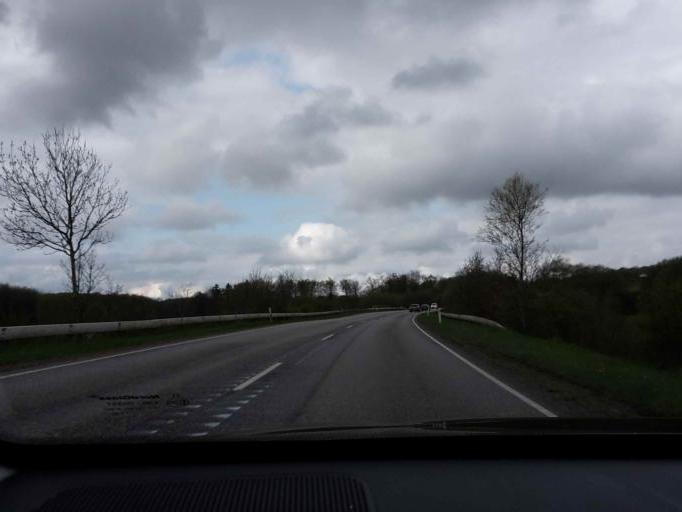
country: DK
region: South Denmark
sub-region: Vejle Kommune
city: Jelling
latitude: 55.6969
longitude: 9.4081
